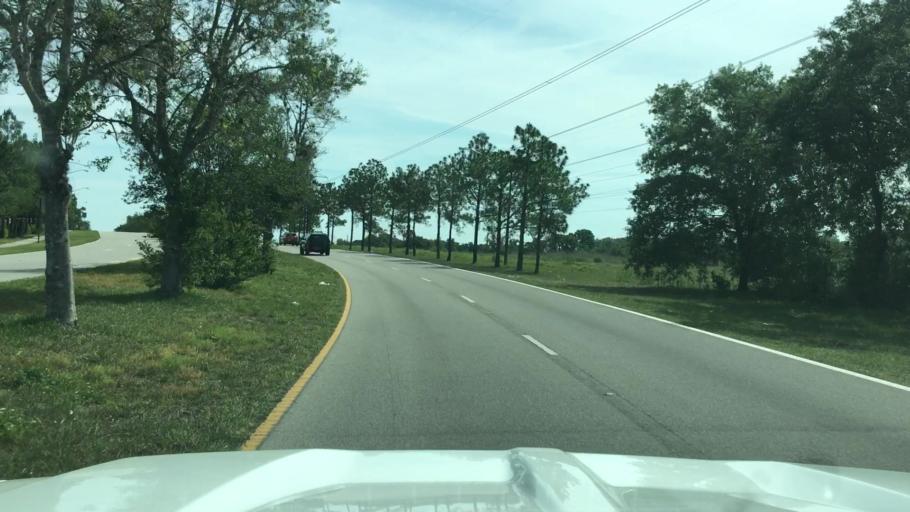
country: US
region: Florida
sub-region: Pasco County
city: Shady Hills
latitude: 28.4381
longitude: -82.5449
